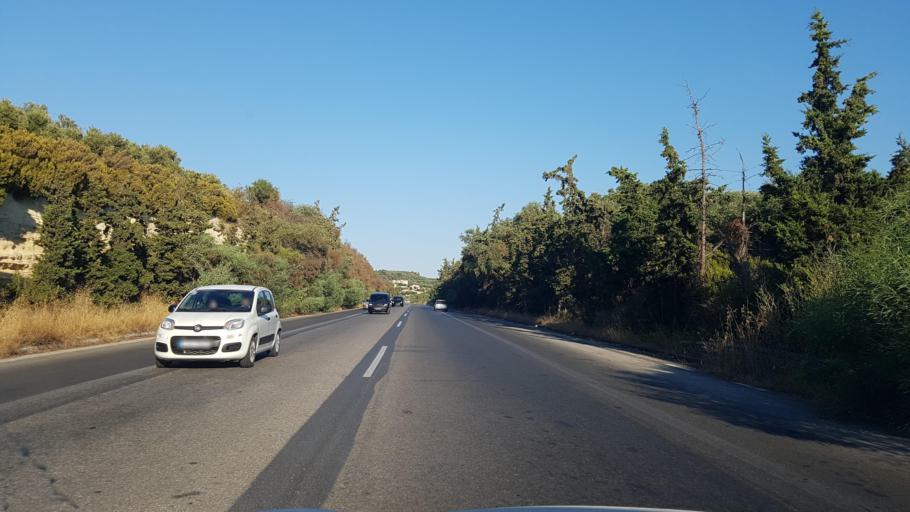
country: GR
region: Crete
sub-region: Nomos Chanias
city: Gerani
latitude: 35.5153
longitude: 23.8481
